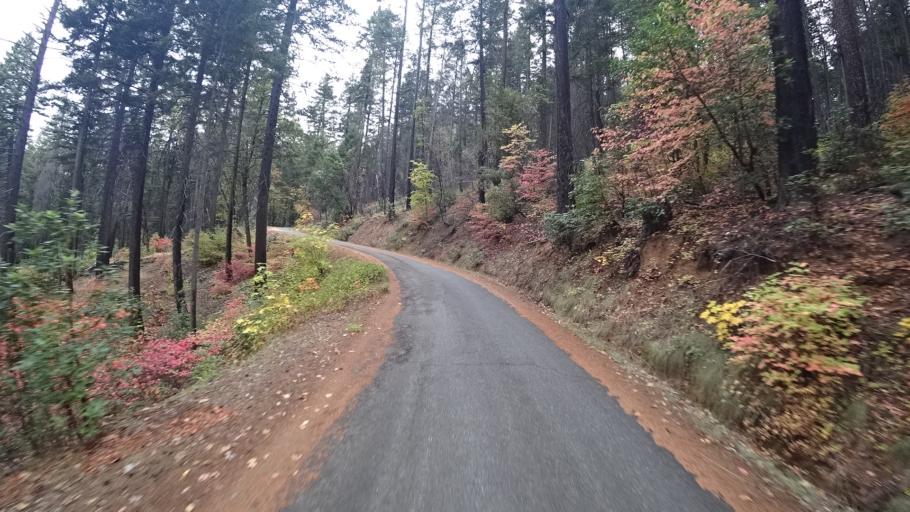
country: US
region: California
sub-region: Siskiyou County
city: Happy Camp
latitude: 41.8139
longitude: -123.3334
